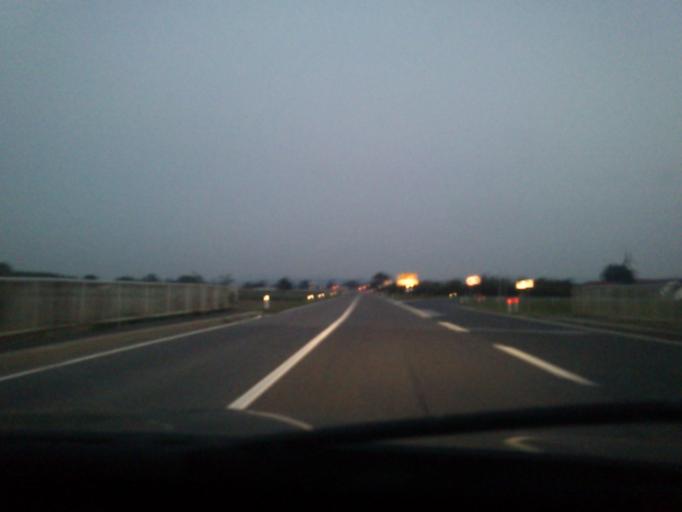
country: SI
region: Hajdina
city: Spodnja Hajdina
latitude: 46.4133
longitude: 15.8355
